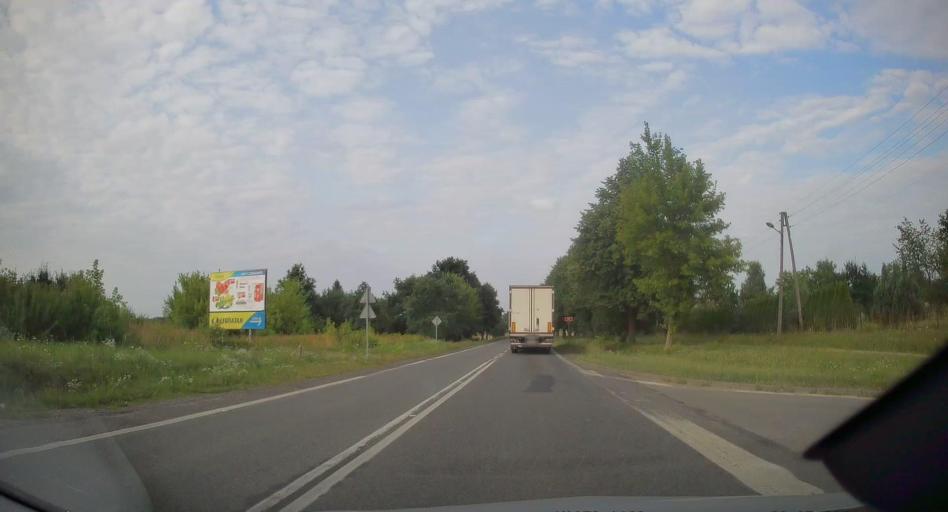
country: PL
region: Silesian Voivodeship
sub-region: Powiat czestochowski
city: Redziny
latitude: 50.8663
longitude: 19.2279
